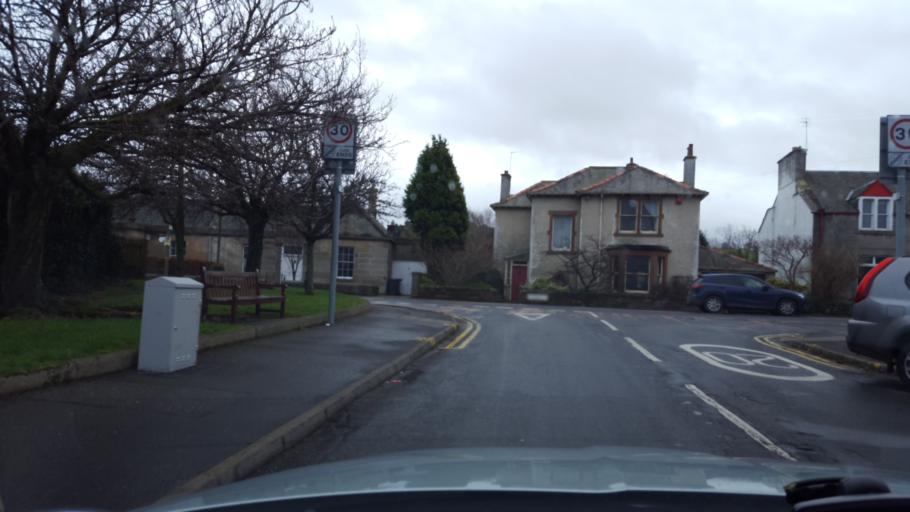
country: GB
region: Scotland
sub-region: Edinburgh
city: Currie
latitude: 55.8975
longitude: -3.3039
